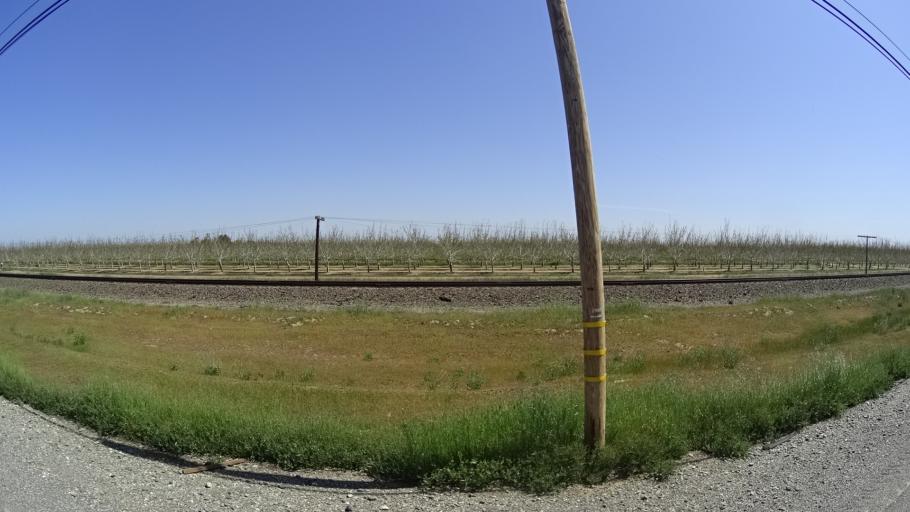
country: US
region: California
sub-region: Glenn County
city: Willows
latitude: 39.6086
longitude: -122.1940
